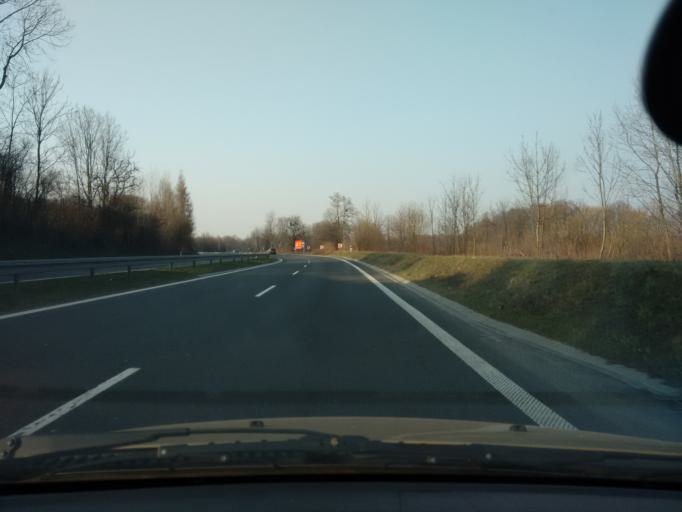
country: PL
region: Silesian Voivodeship
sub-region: Powiat cieszynski
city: Ochaby
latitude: 49.8291
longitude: 18.7876
